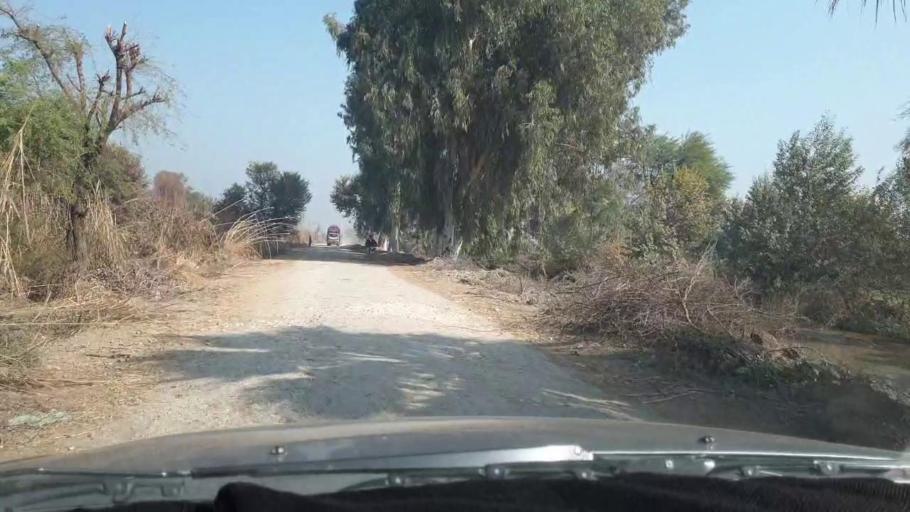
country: PK
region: Sindh
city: Khanpur
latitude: 27.7879
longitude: 69.5551
